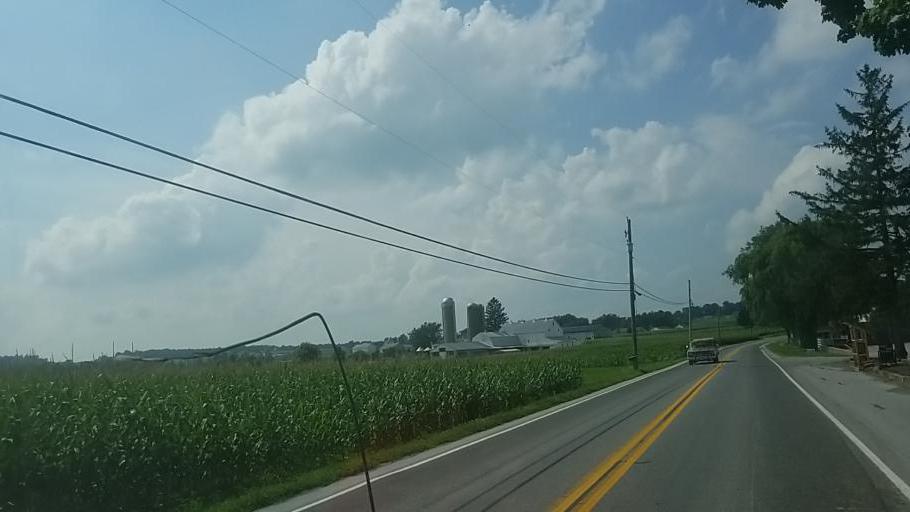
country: US
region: Pennsylvania
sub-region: Lancaster County
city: Georgetown
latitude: 39.9474
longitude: -76.0934
